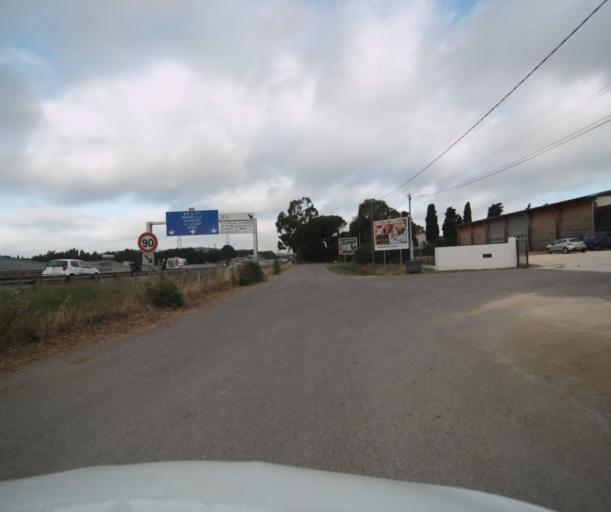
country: FR
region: Provence-Alpes-Cote d'Azur
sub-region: Departement du Var
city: Ollioules
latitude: 43.1197
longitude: 5.8599
